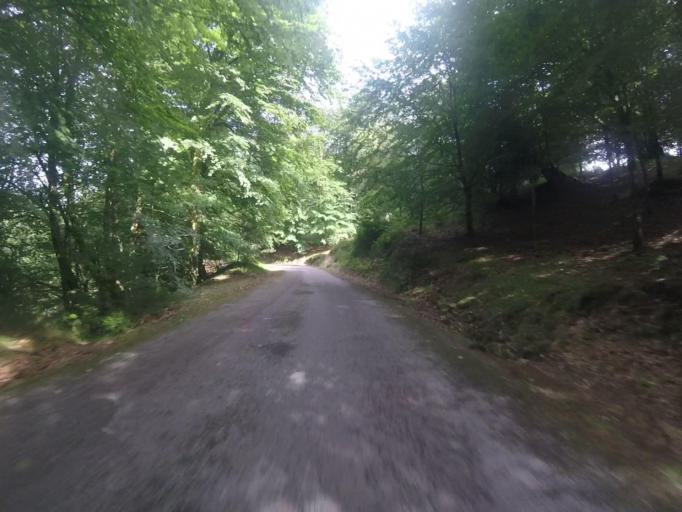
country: ES
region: Navarre
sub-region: Provincia de Navarra
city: Goizueta
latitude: 43.2284
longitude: -1.8055
